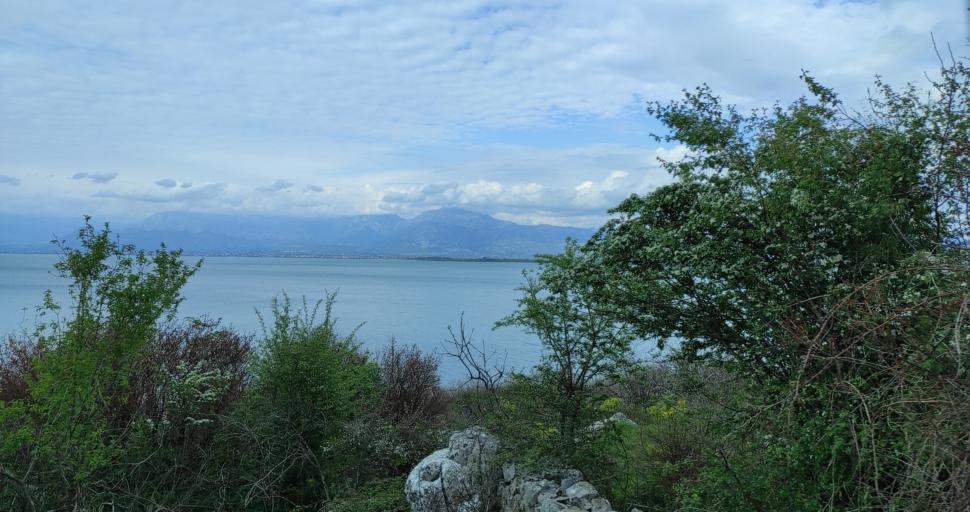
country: AL
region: Shkoder
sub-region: Rrethi i Shkodres
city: Berdica e Madhe
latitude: 42.0658
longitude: 19.4302
